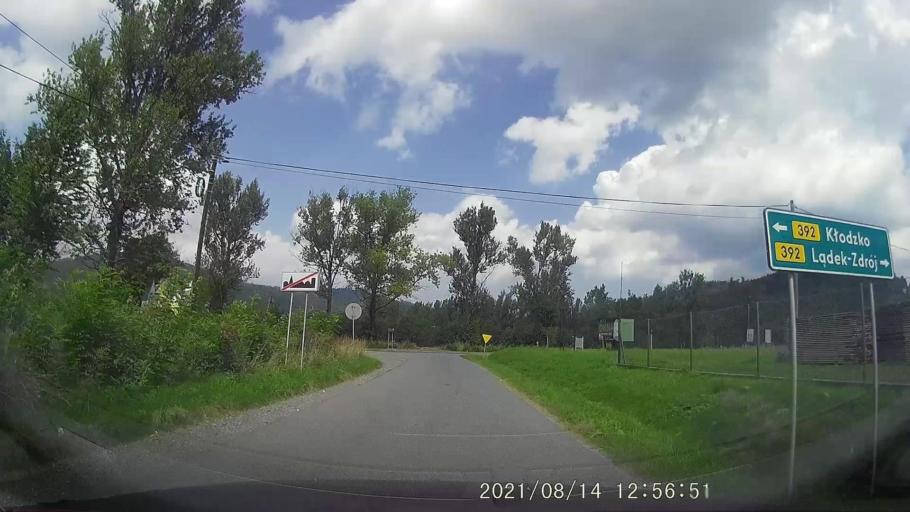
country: PL
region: Lower Silesian Voivodeship
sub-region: Powiat klodzki
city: Ladek-Zdroj
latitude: 50.3404
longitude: 16.8334
